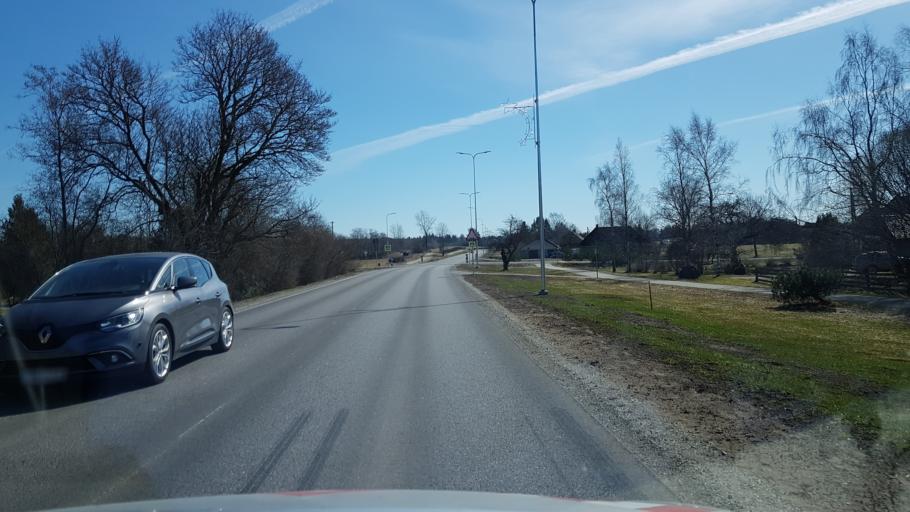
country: EE
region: Laeaene-Virumaa
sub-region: Vinni vald
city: Vinni
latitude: 59.2816
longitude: 26.4208
